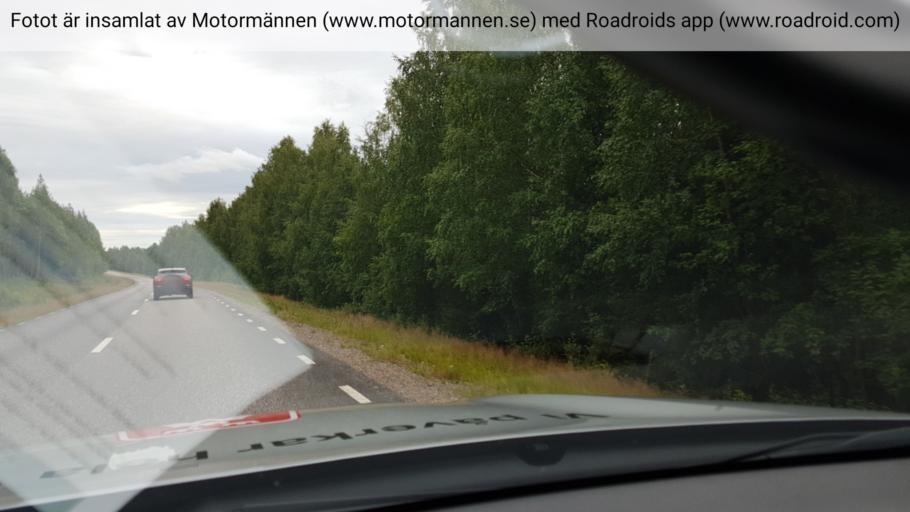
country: SE
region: Norrbotten
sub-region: Overkalix Kommun
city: OEverkalix
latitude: 66.5456
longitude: 22.7548
